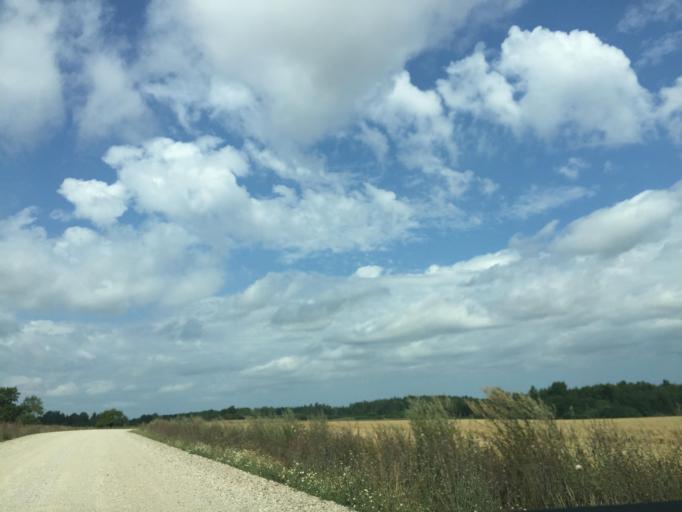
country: LV
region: Kandava
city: Kandava
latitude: 57.0002
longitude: 22.8602
